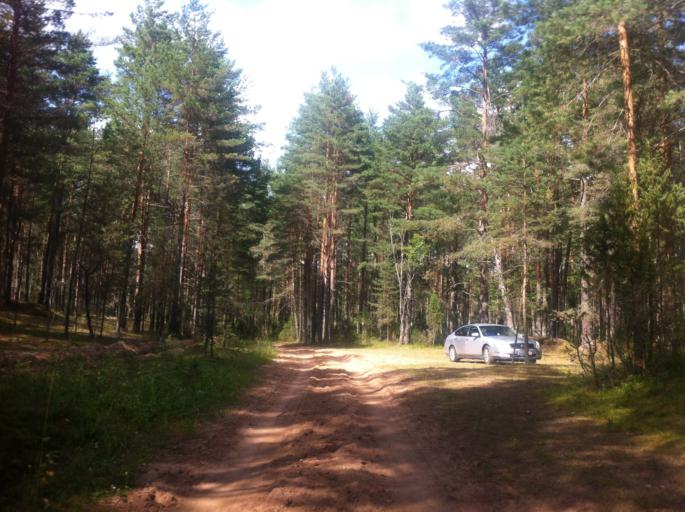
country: RU
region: Pskov
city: Izborsk
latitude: 57.8311
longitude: 27.9377
